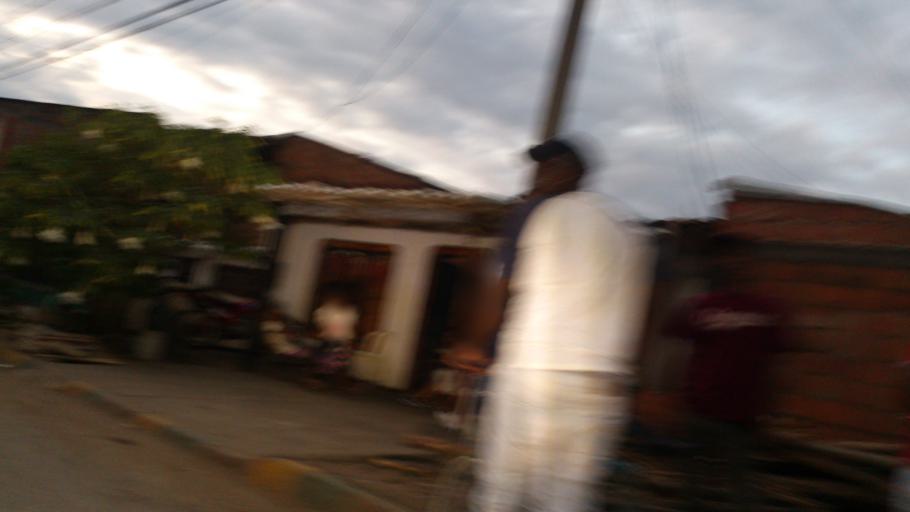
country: CO
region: Valle del Cauca
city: Jamundi
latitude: 3.2633
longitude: -76.5370
